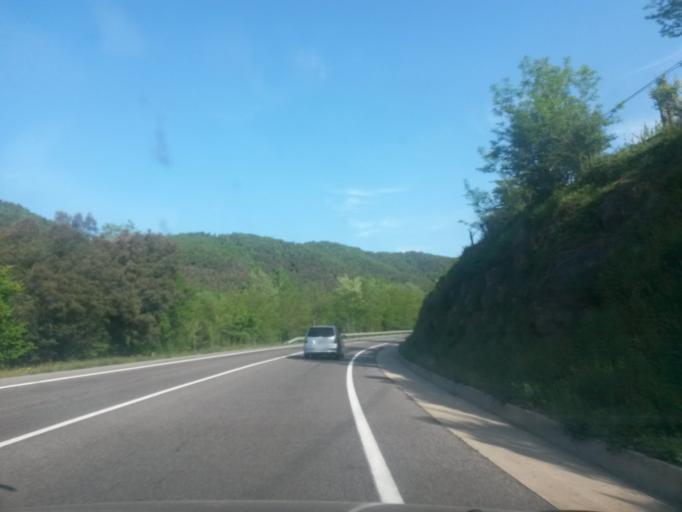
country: ES
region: Catalonia
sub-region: Provincia de Girona
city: Sant Feliu de Pallerols
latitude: 42.1041
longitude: 2.4932
